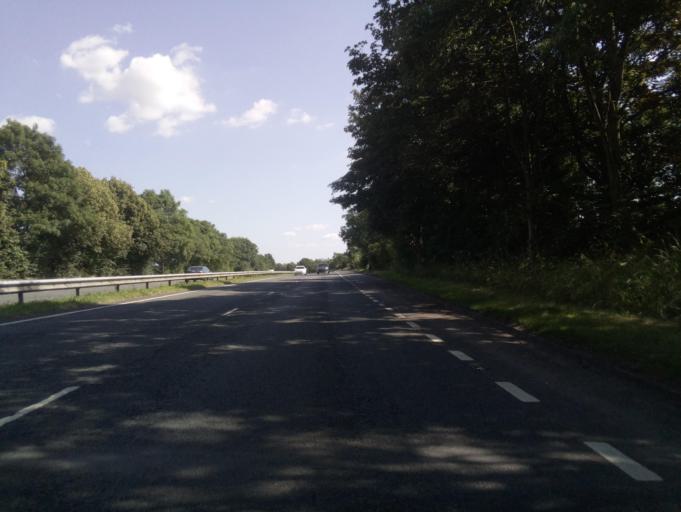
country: GB
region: England
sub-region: Worcestershire
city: Barnt Green
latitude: 52.3199
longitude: -2.0021
